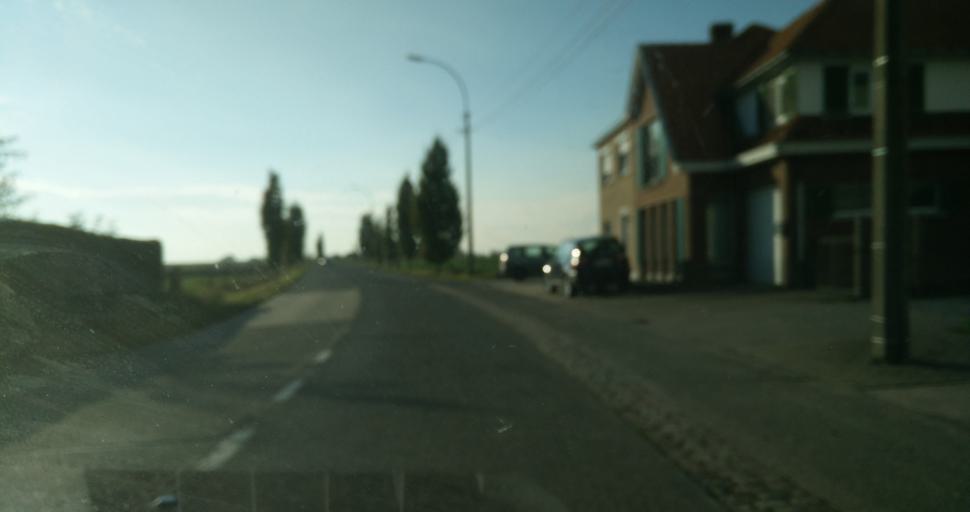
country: BE
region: Flanders
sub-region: Provincie Oost-Vlaanderen
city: Oosterzele
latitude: 50.9280
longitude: 3.8132
